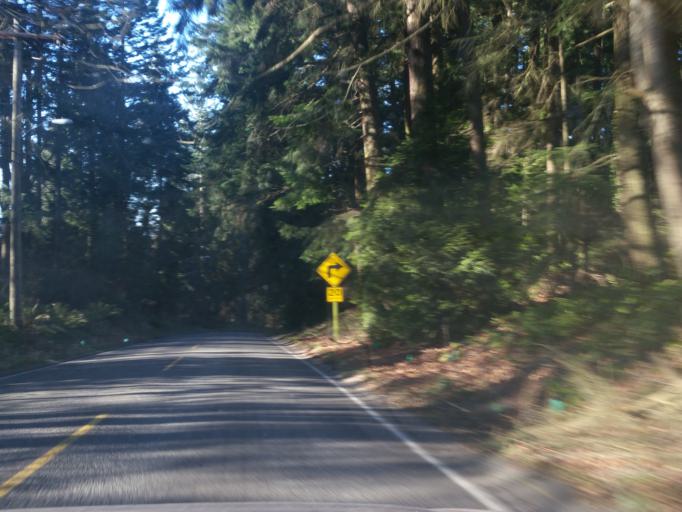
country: US
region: Washington
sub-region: Snohomish County
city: Meadowdale
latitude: 47.8492
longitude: -122.3259
